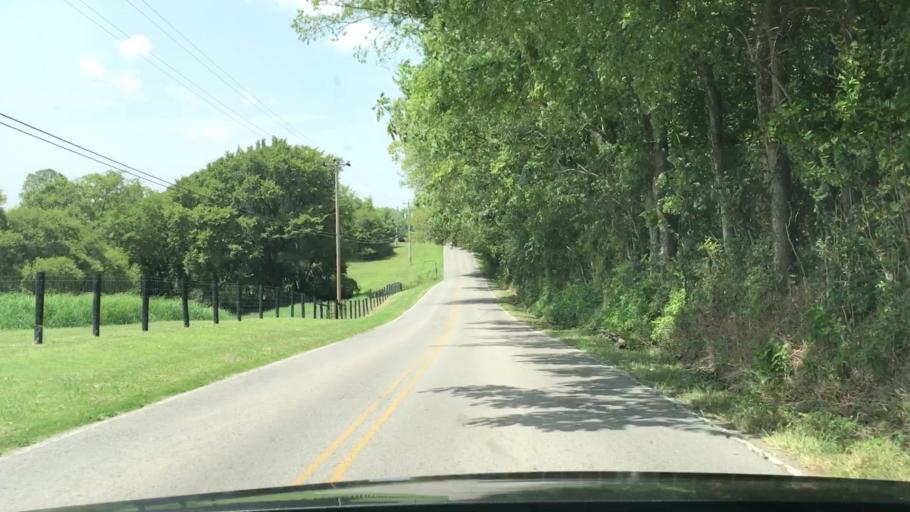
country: US
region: Tennessee
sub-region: Rutherford County
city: La Vergne
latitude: 35.9672
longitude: -86.6093
